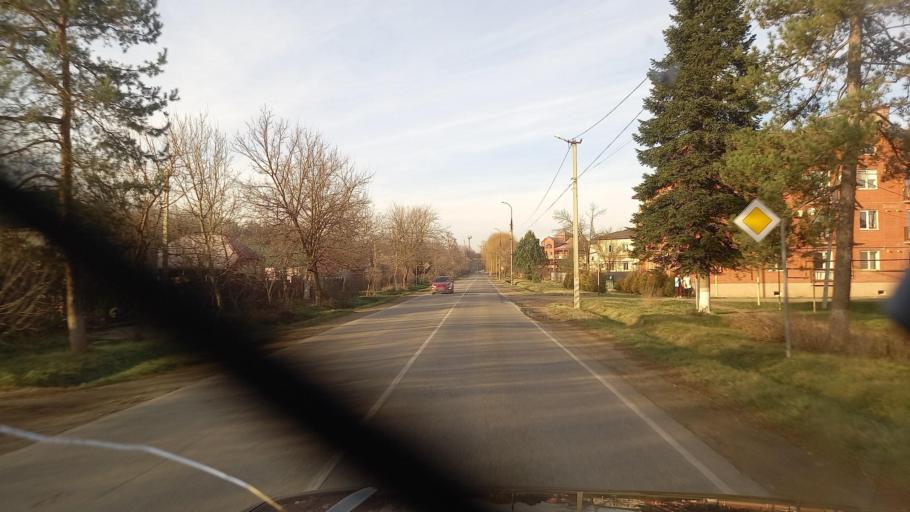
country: RU
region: Krasnodarskiy
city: Khadyzhensk
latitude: 44.4380
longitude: 39.5266
